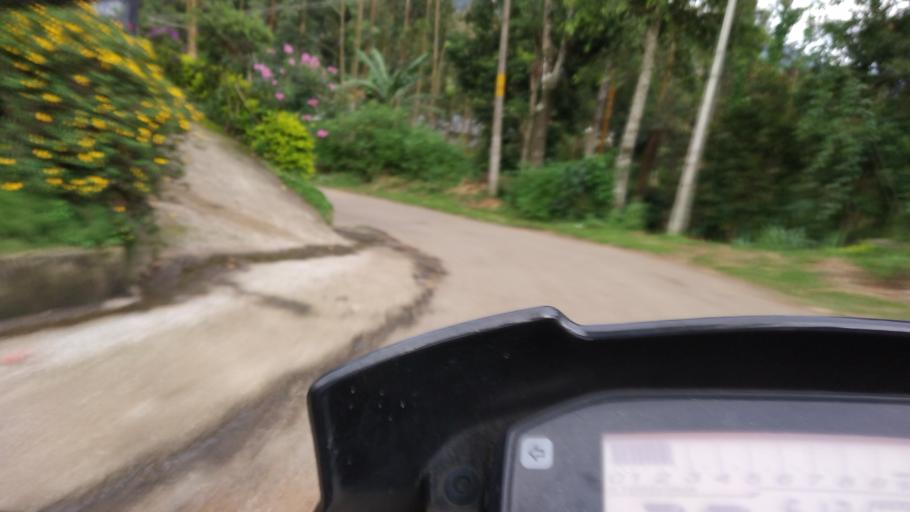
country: IN
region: Tamil Nadu
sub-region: Theni
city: Bodinayakkanur
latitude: 10.0240
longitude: 77.2430
